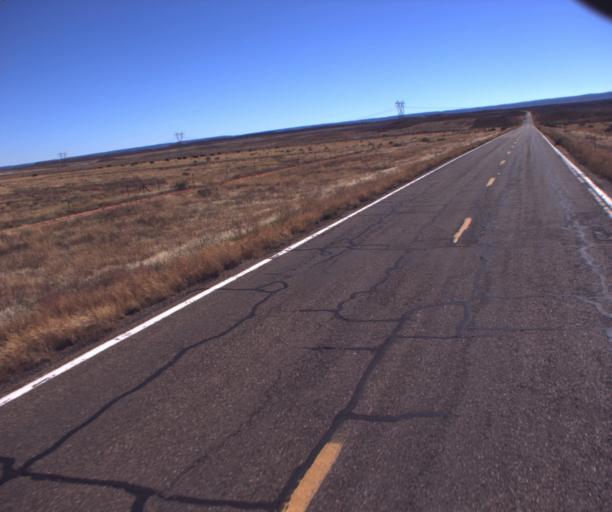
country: US
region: Arizona
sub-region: Coconino County
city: Fredonia
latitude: 36.9198
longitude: -112.4360
